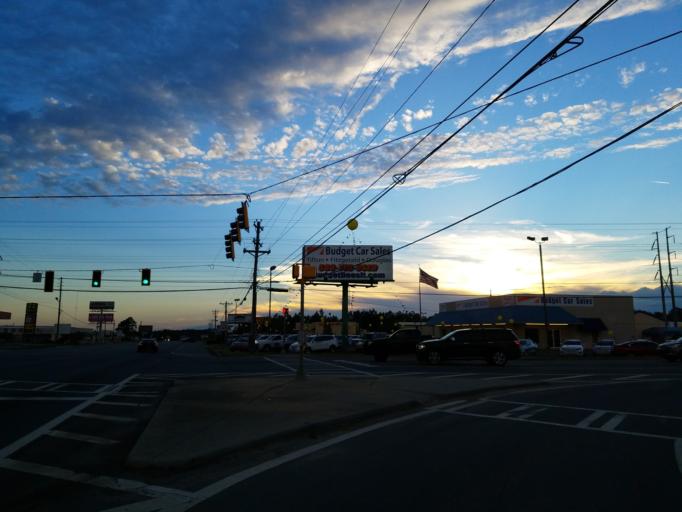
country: US
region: Georgia
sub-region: Tift County
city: Unionville
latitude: 31.4447
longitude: -83.5467
